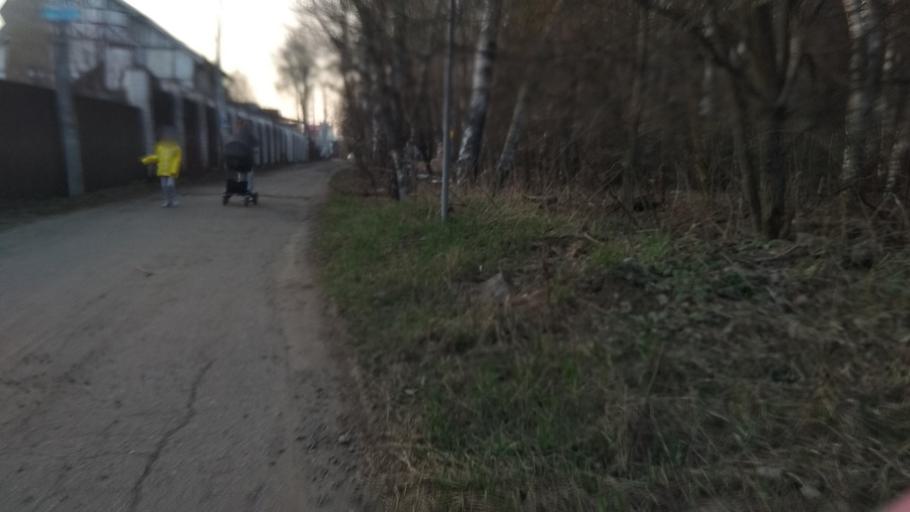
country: RU
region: Moskovskaya
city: Razvilka
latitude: 55.5721
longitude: 37.7441
